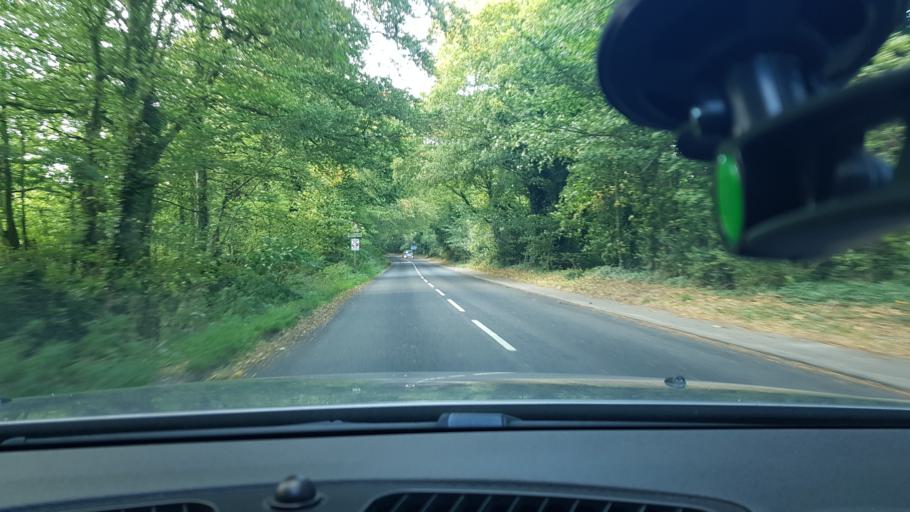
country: GB
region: England
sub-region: West Berkshire
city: Lambourn
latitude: 51.5124
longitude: -1.5364
